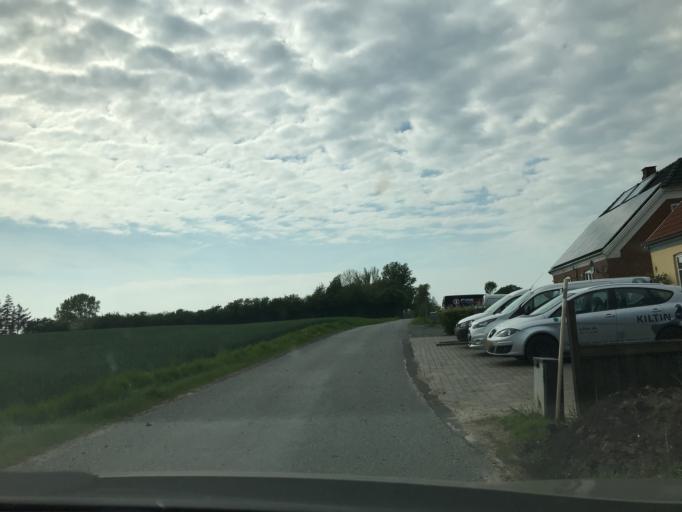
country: DK
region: South Denmark
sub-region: Middelfart Kommune
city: Ejby
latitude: 55.3546
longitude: 9.8965
